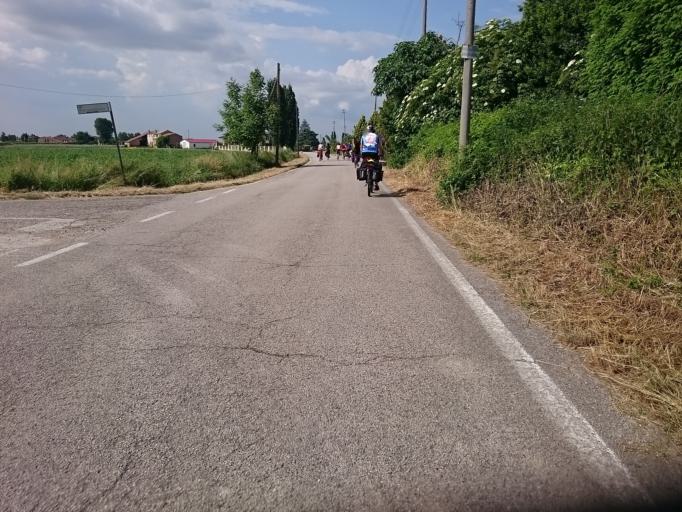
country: IT
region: Veneto
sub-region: Provincia di Padova
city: Casale di Scodosia
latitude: 45.1991
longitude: 11.4802
